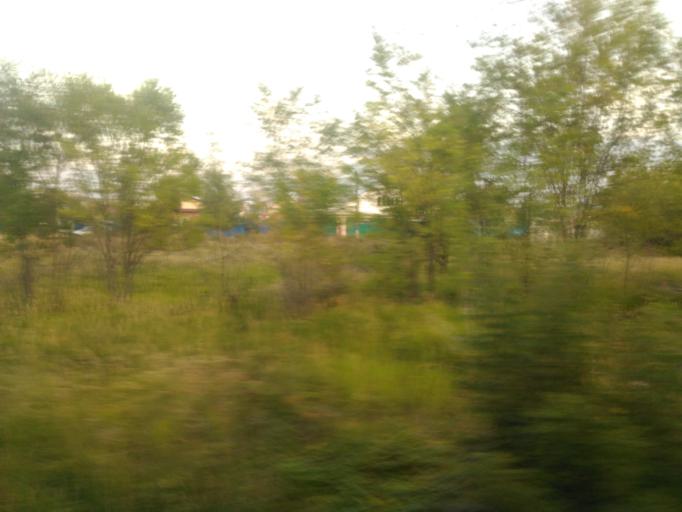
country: RU
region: Ulyanovsk
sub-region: Ulyanovskiy Rayon
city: Ulyanovsk
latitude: 54.2659
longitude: 48.2825
